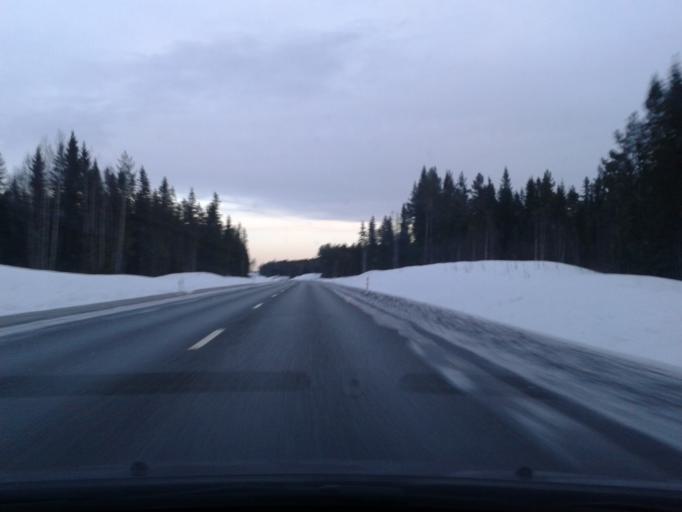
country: SE
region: Vaesternorrland
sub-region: Kramfors Kommun
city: Bollstabruk
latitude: 63.0717
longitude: 17.5663
